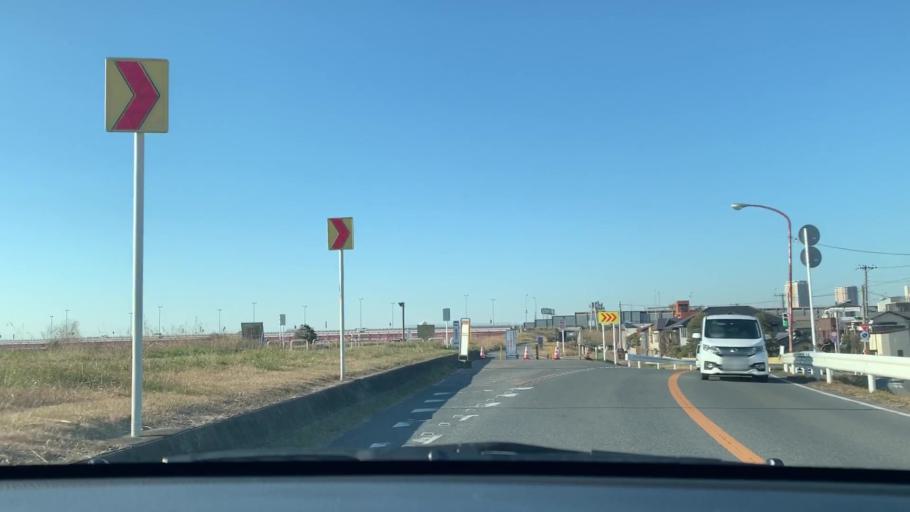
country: JP
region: Tokyo
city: Urayasu
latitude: 35.7078
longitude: 139.9191
